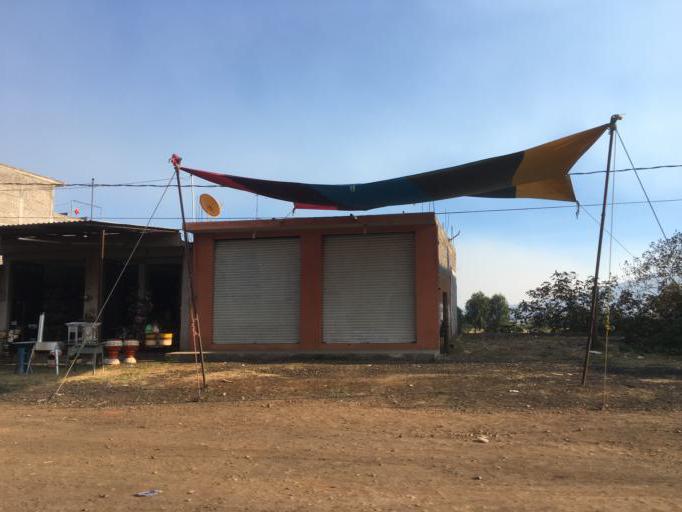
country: MX
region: Michoacan
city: Santa Fe de la Laguna
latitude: 19.6711
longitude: -101.5555
